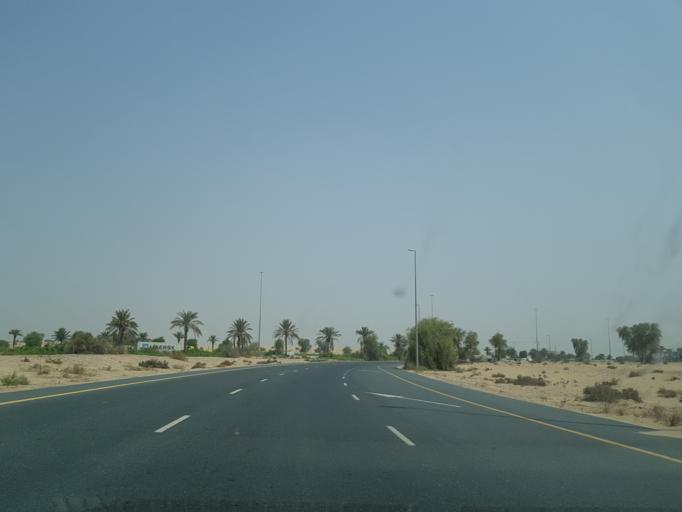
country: AE
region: Dubai
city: Dubai
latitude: 25.0645
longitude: 55.2965
